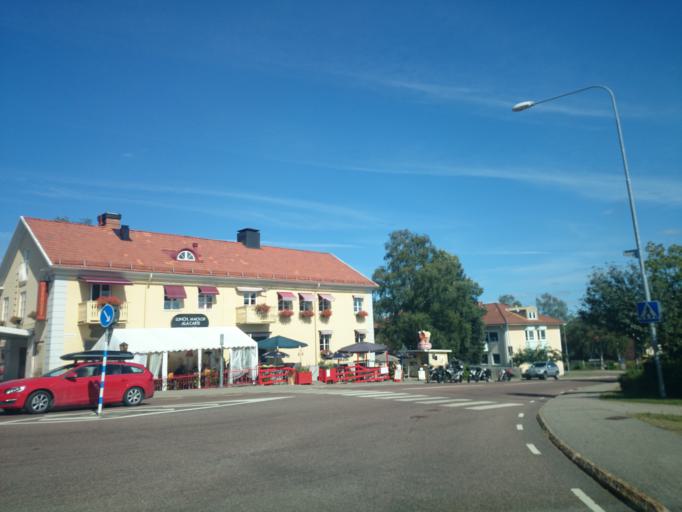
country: SE
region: Gaevleborg
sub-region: Ljusdals Kommun
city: Jaervsoe
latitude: 61.7133
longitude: 16.1690
